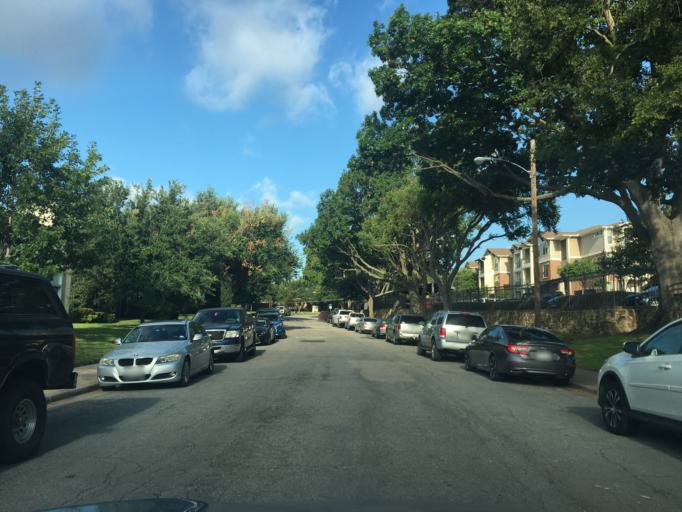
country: US
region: Texas
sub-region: Dallas County
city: Highland Park
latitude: 32.8443
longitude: -96.7635
